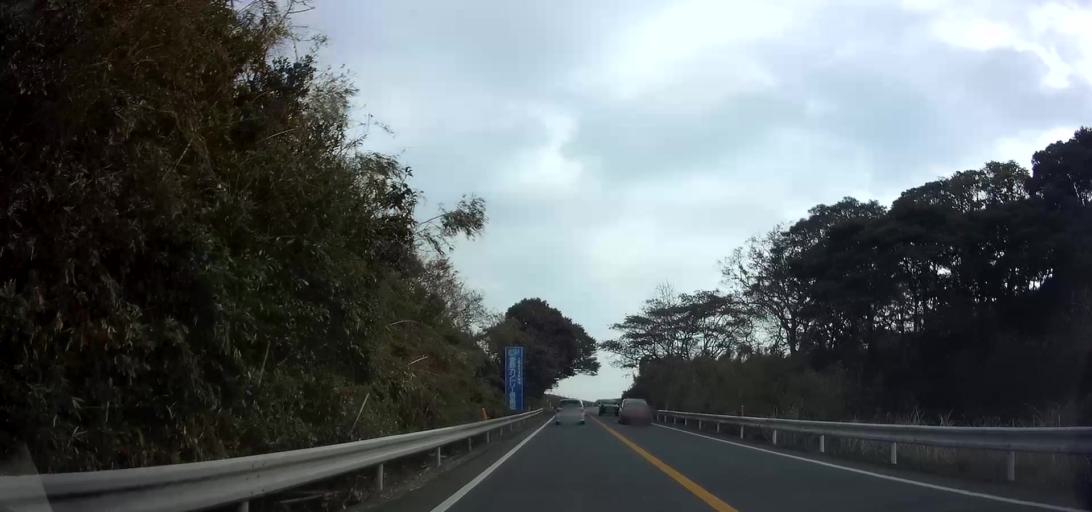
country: JP
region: Nagasaki
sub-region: Isahaya-shi
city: Isahaya
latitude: 32.7979
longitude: 130.1462
